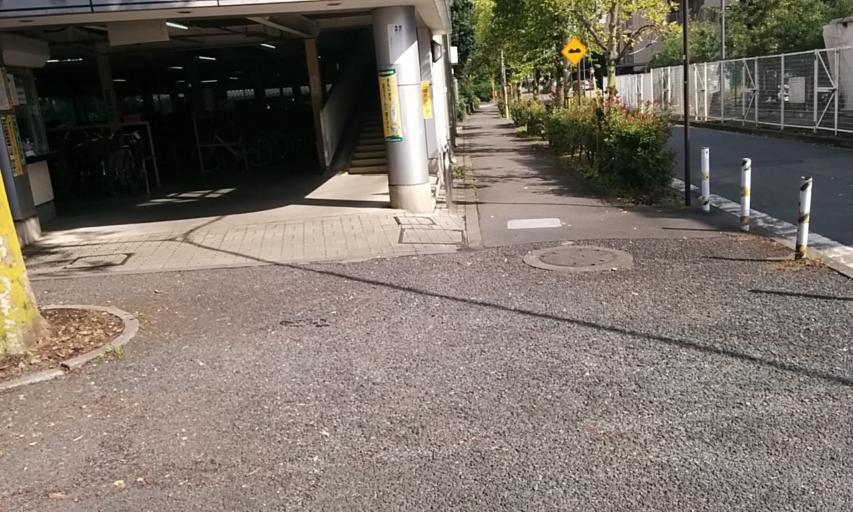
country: JP
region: Tokyo
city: Kokubunji
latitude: 35.6802
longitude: 139.4724
